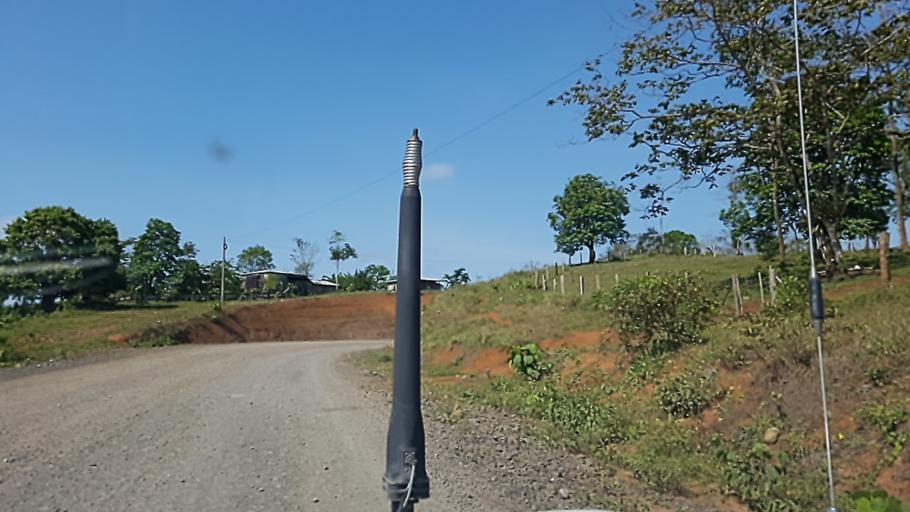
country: NI
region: Atlantico Sur
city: Nueva Guinea
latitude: 11.7849
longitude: -84.1667
